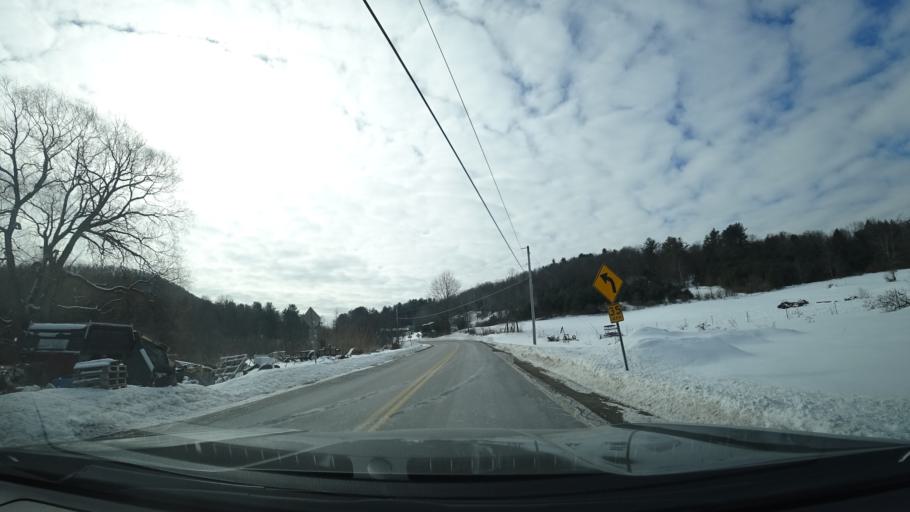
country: US
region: New York
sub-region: Washington County
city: Greenwich
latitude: 43.2419
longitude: -73.3809
